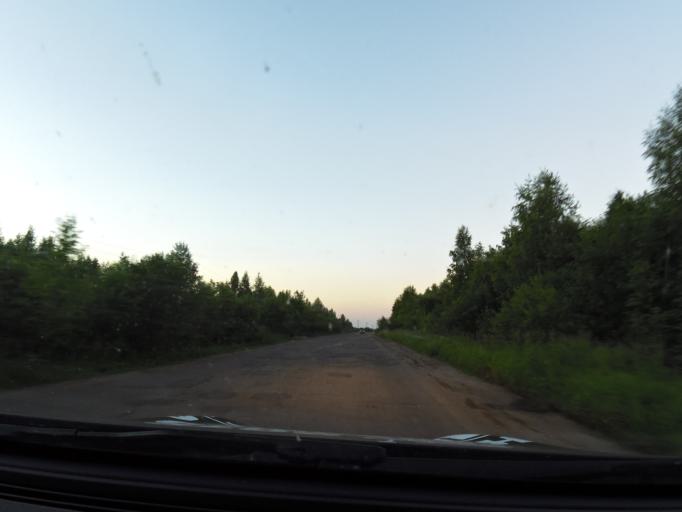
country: RU
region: Kostroma
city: Buy
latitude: 58.4285
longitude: 41.2839
